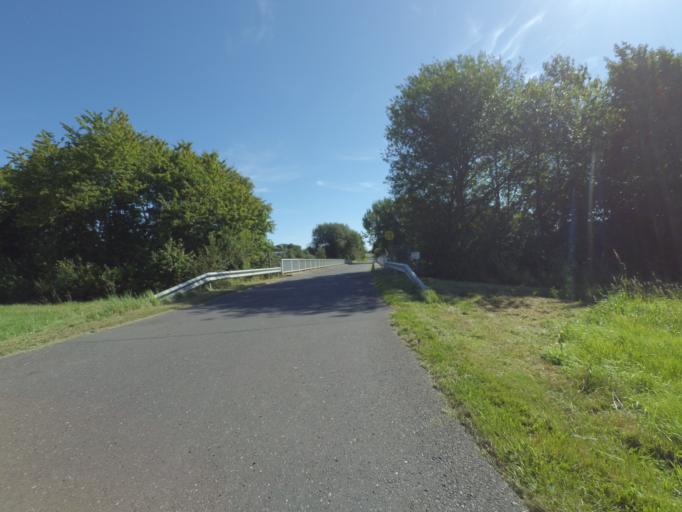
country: DE
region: Rheinland-Pfalz
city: Laufeld
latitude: 50.0822
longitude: 6.8715
